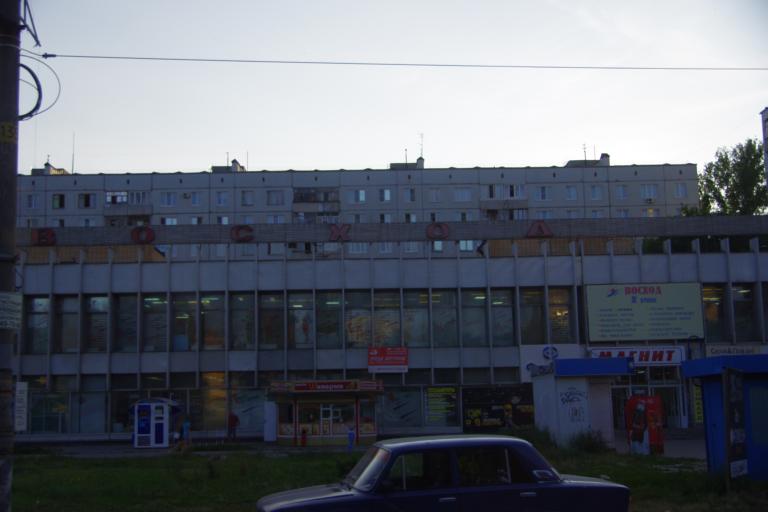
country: RU
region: Samara
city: Tol'yatti
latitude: 53.5310
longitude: 49.2766
